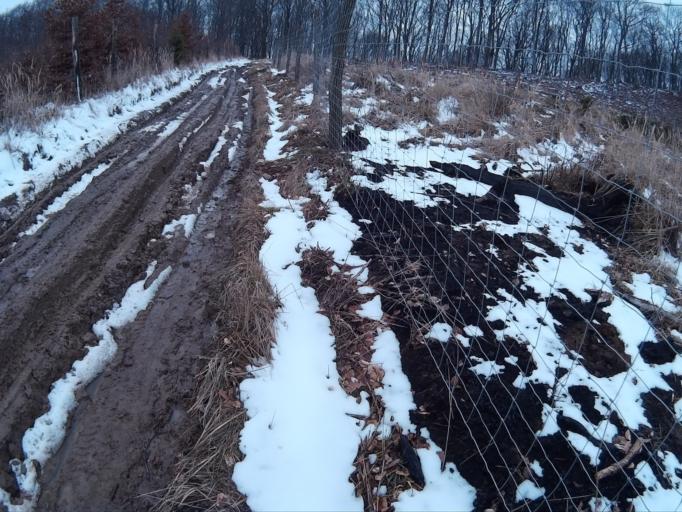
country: HU
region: Borsod-Abauj-Zemplen
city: Gonc
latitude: 48.4184
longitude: 21.3594
